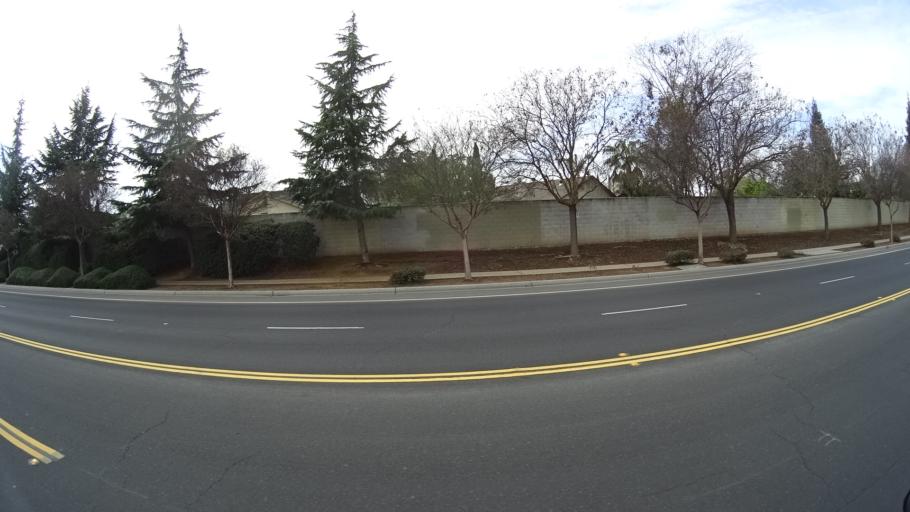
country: US
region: California
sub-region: Fresno County
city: West Park
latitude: 36.8327
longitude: -119.8795
